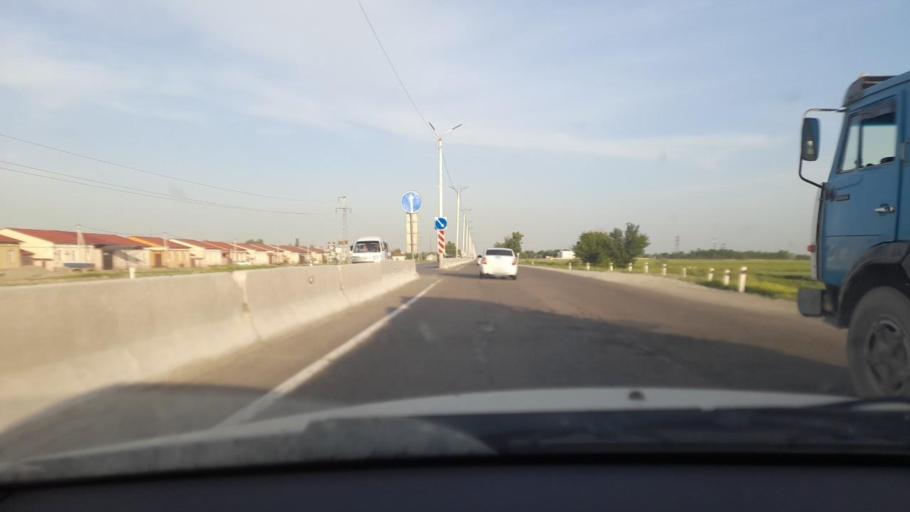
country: KZ
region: Ongtustik Qazaqstan
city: Myrzakent
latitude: 40.5535
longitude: 68.3963
